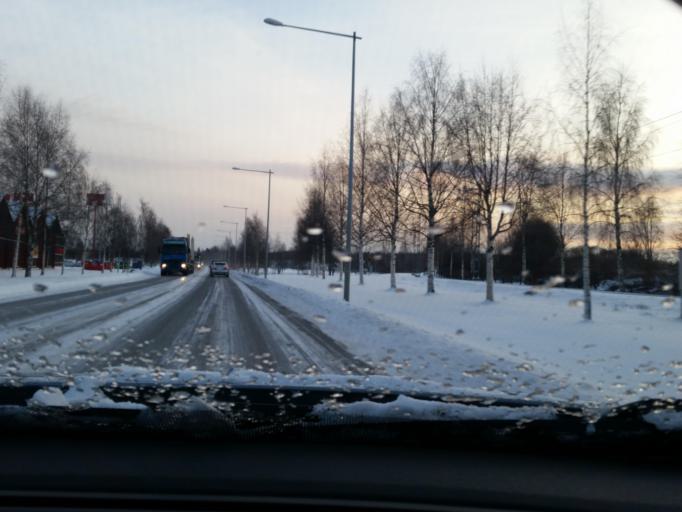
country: SE
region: Norrbotten
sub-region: Pitea Kommun
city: Pitea
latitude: 65.3147
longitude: 21.4781
